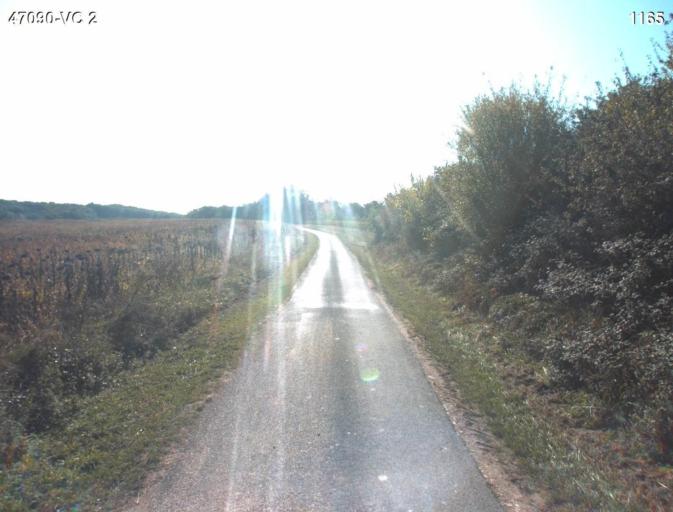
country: FR
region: Aquitaine
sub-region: Departement du Lot-et-Garonne
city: Vianne
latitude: 44.1815
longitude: 0.3678
